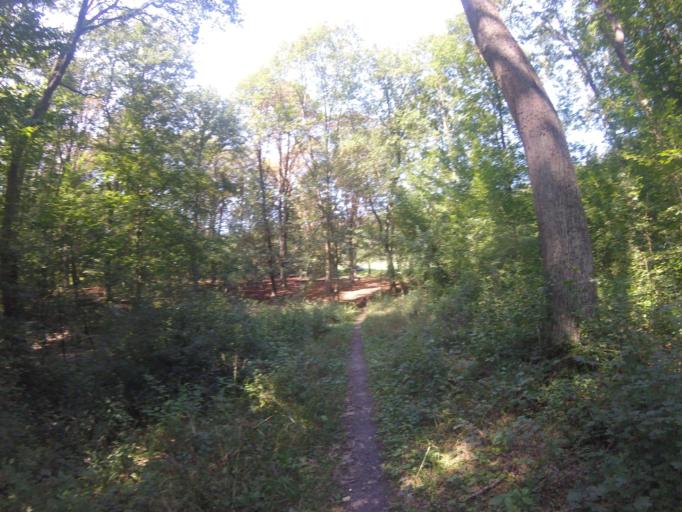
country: HU
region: Nograd
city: Bujak
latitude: 47.9003
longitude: 19.5164
